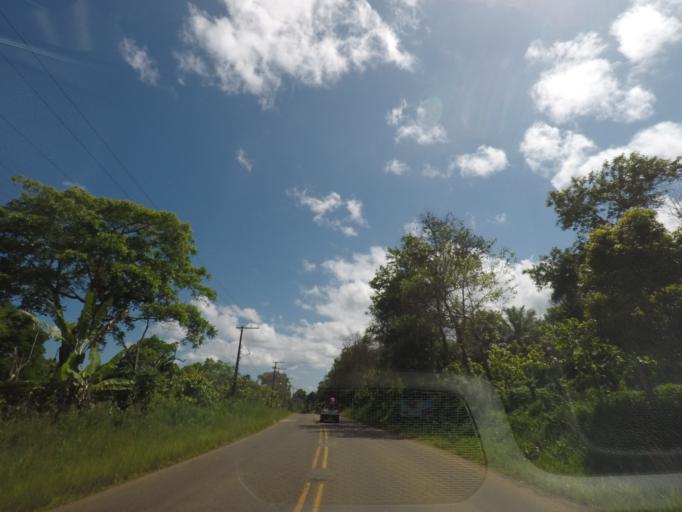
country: BR
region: Bahia
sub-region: Taperoa
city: Taperoa
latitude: -13.5277
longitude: -39.1041
